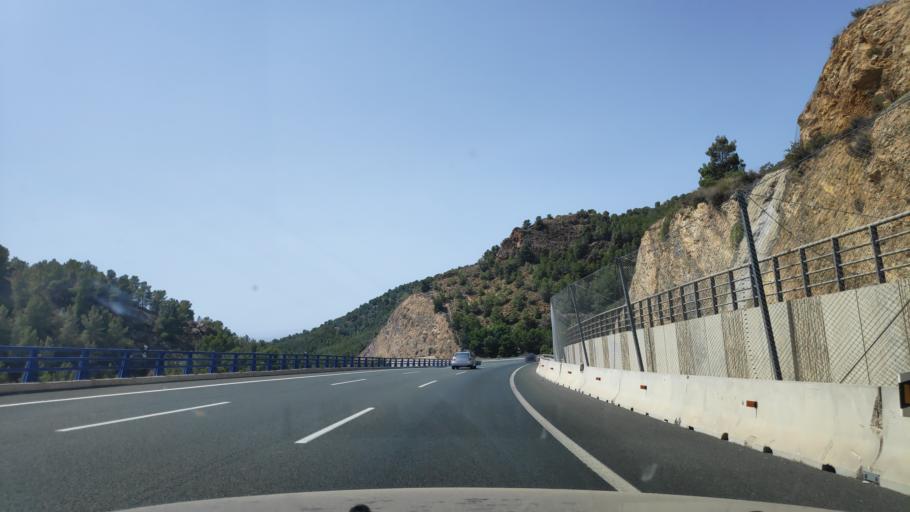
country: ES
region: Murcia
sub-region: Murcia
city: Murcia
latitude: 37.9035
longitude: -1.1450
